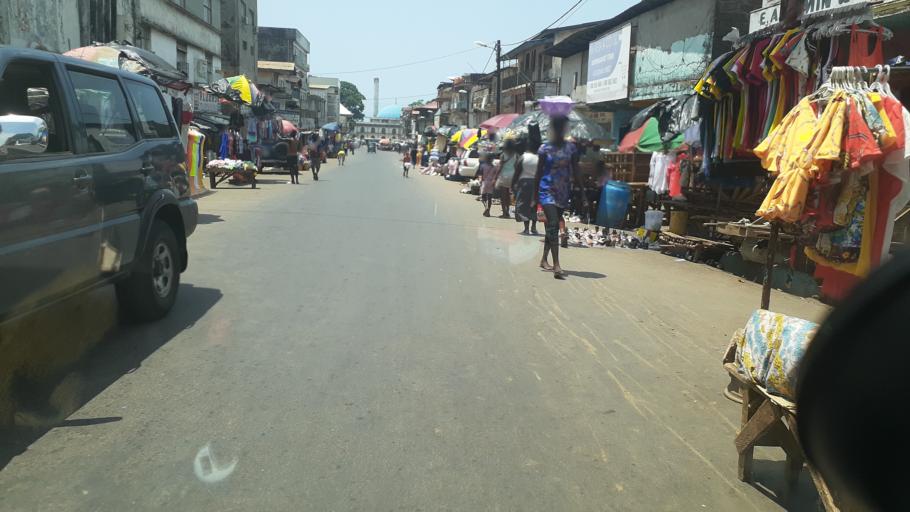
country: SL
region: Western Area
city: Freetown
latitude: 8.4890
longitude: -13.2308
